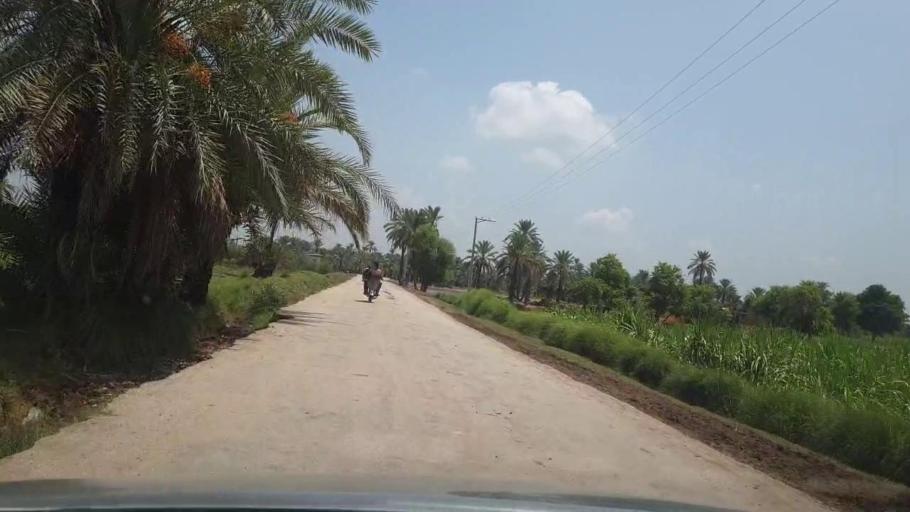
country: PK
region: Sindh
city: Pir jo Goth
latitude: 27.6014
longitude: 68.6026
